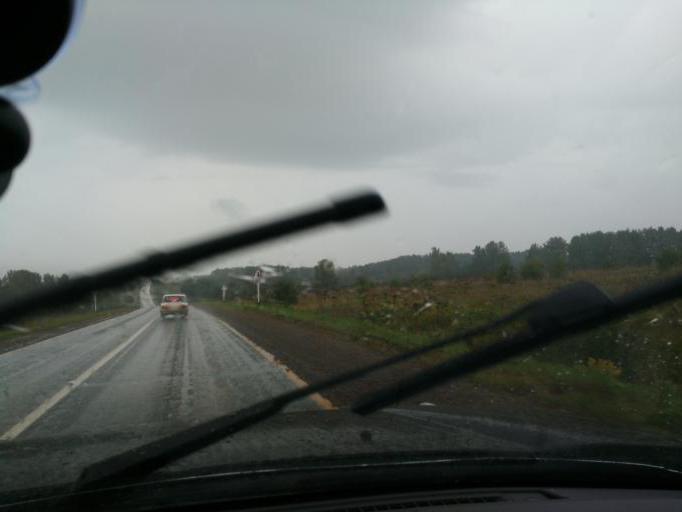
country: RU
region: Perm
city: Osa
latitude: 57.1440
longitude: 55.5289
